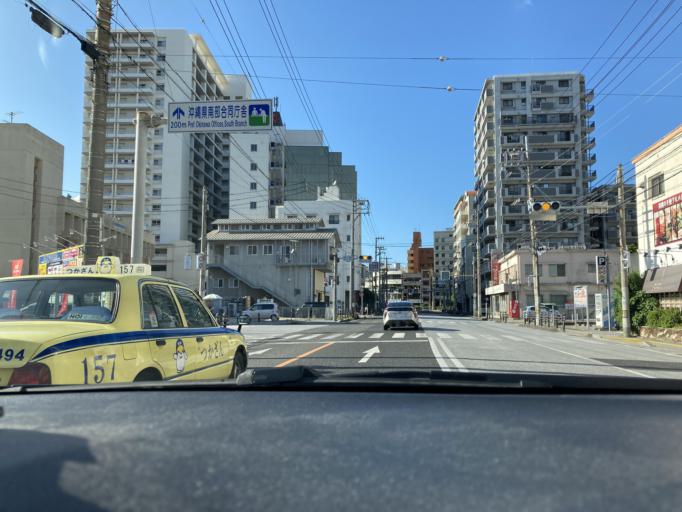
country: JP
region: Okinawa
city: Naha-shi
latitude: 26.2086
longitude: 127.6789
